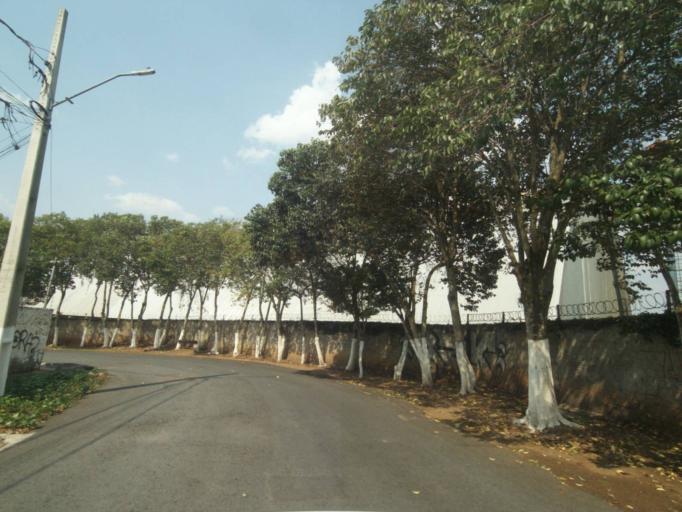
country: BR
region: Parana
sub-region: Sao Jose Dos Pinhais
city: Sao Jose dos Pinhais
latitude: -25.5399
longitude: -49.2385
